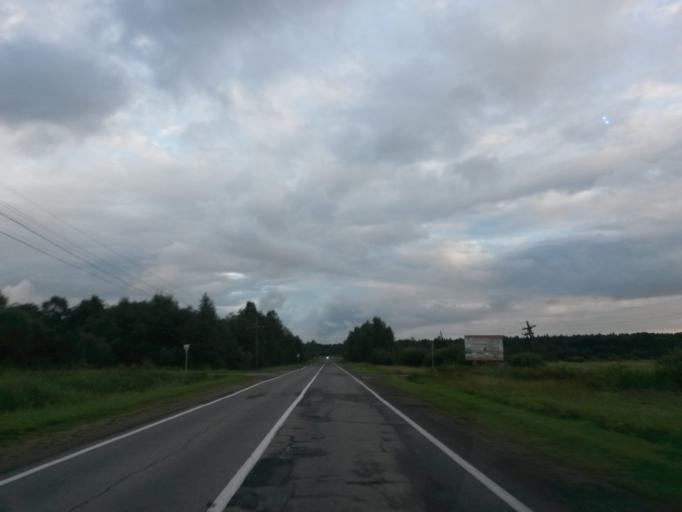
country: RU
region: Jaroslavl
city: Tutayev
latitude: 57.9332
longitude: 39.5022
